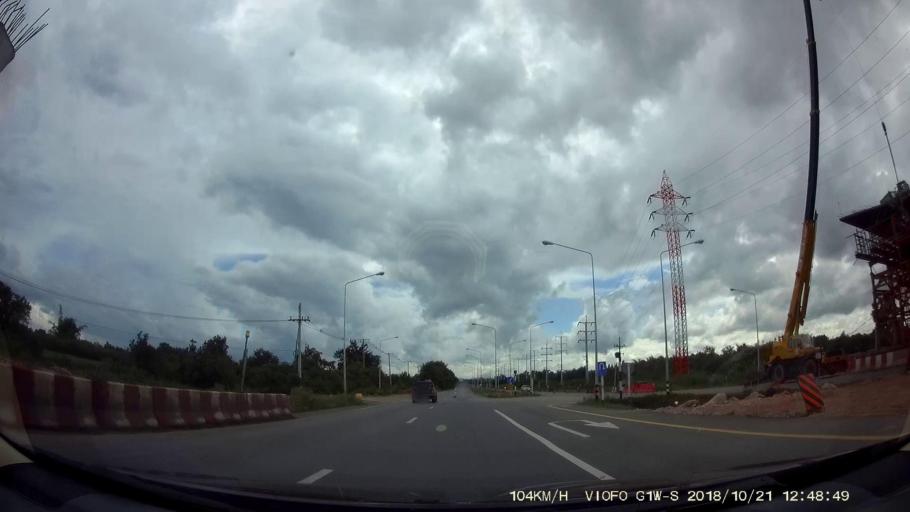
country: TH
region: Nakhon Ratchasima
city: Amphoe Sikhiu
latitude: 14.9064
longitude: 101.6841
